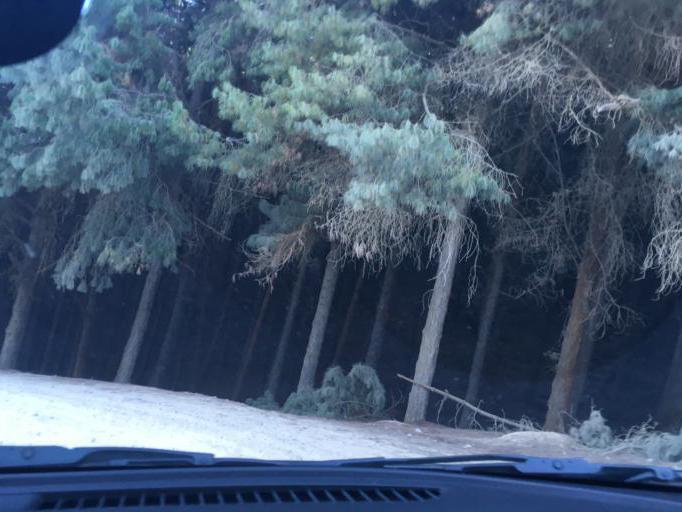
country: CO
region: Boyaca
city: Aquitania
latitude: 5.5084
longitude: -72.9696
